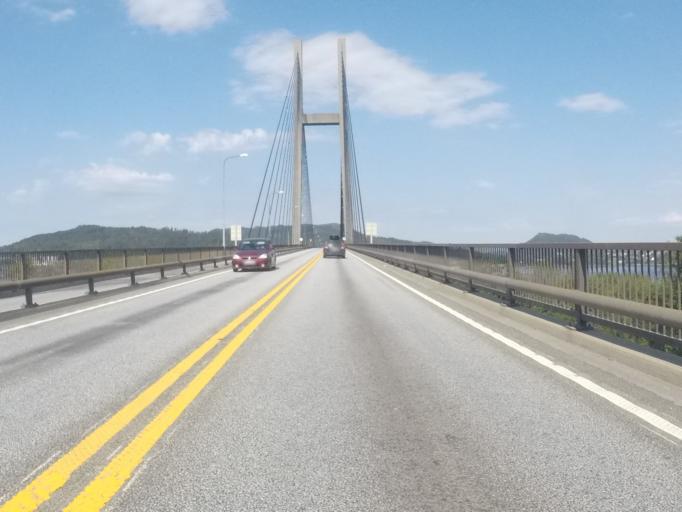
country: NO
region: Hordaland
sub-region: Lindas
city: Knarvik
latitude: 60.5193
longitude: 5.2758
